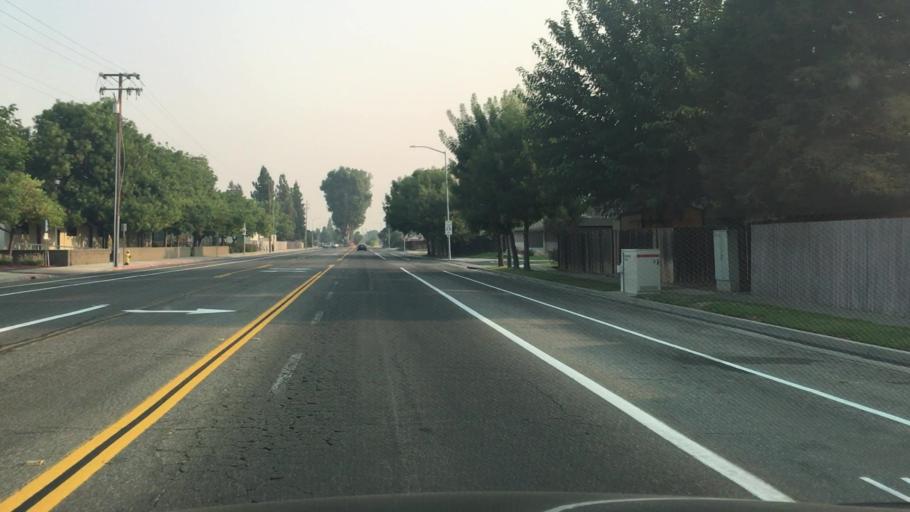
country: US
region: California
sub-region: Fresno County
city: Clovis
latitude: 36.8305
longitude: -119.6729
